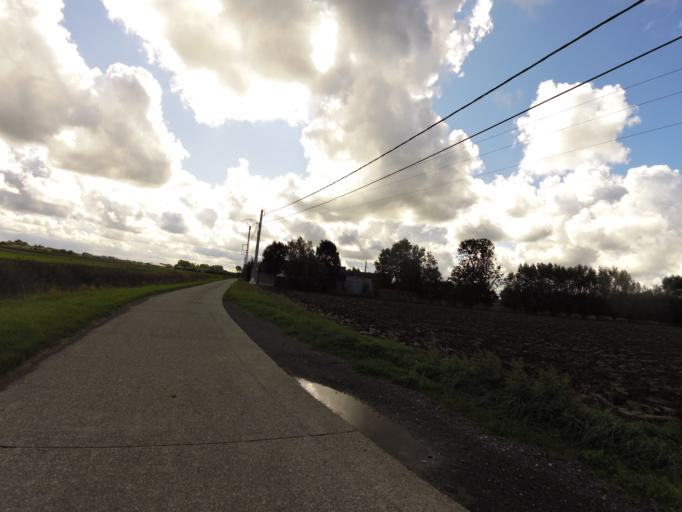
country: BE
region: Flanders
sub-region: Provincie West-Vlaanderen
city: Ostend
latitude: 51.1694
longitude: 2.9054
